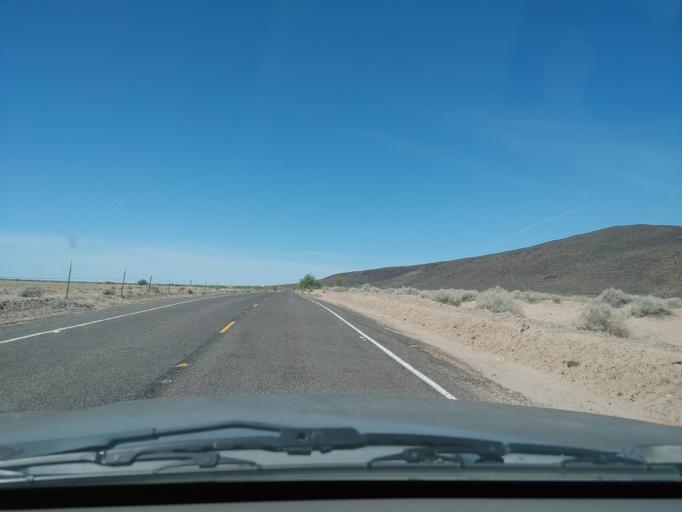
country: US
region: Arizona
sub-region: Maricopa County
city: Gila Bend
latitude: 32.9864
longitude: -113.3080
